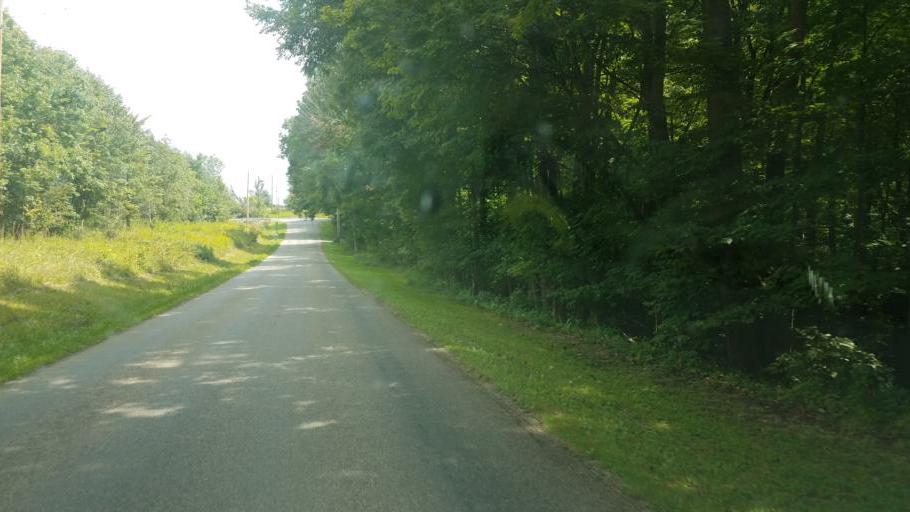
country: US
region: Ohio
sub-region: Knox County
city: Gambier
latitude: 40.3994
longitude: -82.4121
